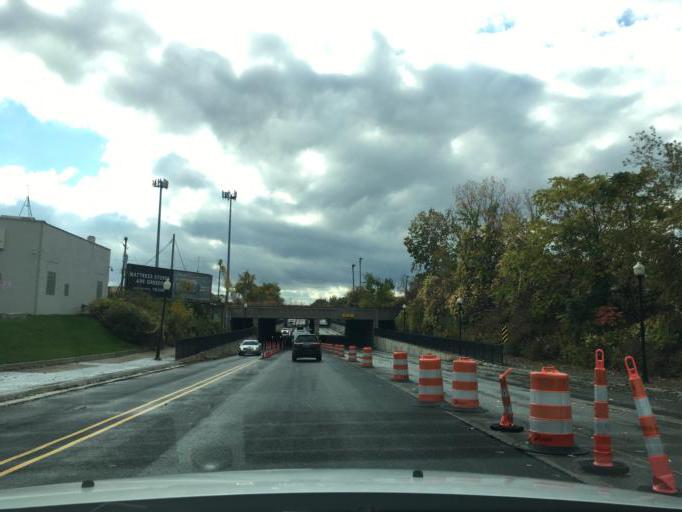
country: US
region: Michigan
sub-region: Wayne County
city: Dearborn
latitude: 42.3164
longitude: -83.1757
